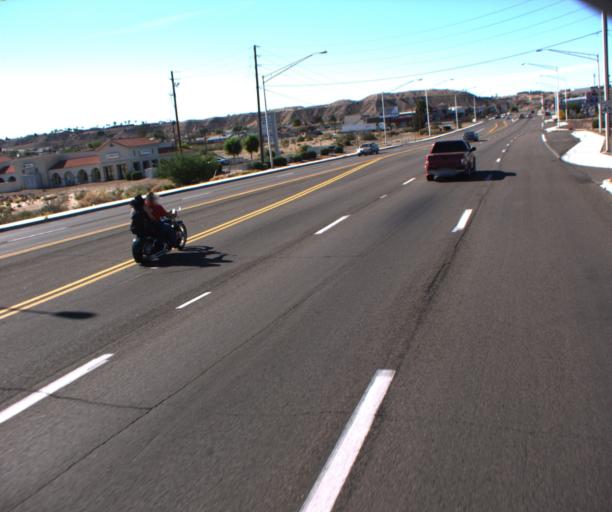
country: US
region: Arizona
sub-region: Mohave County
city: Bullhead City
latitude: 35.0549
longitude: -114.5893
